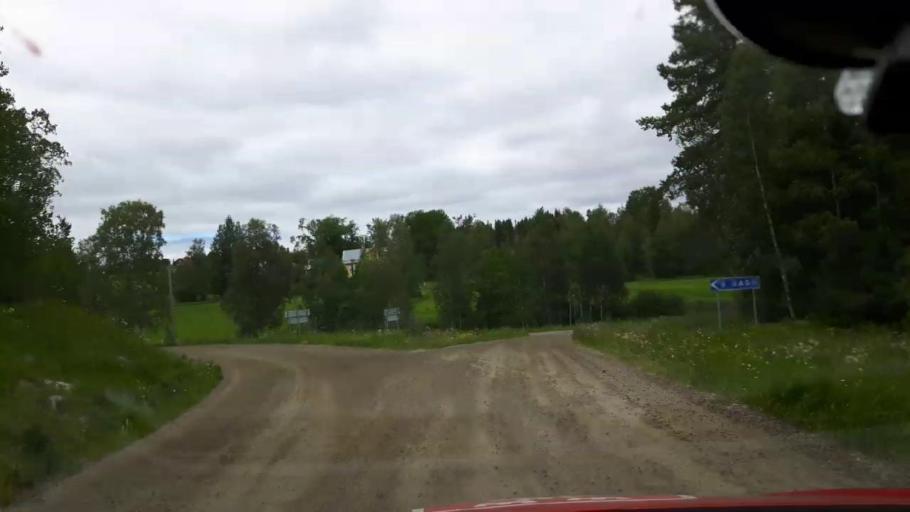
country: SE
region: Jaemtland
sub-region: OEstersunds Kommun
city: Brunflo
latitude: 62.9452
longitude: 14.9839
